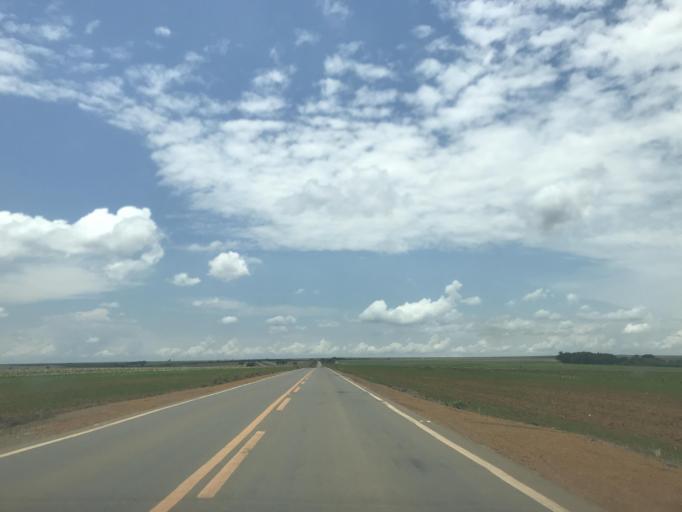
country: BR
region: Goias
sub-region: Luziania
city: Luziania
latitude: -16.4985
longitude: -48.2051
